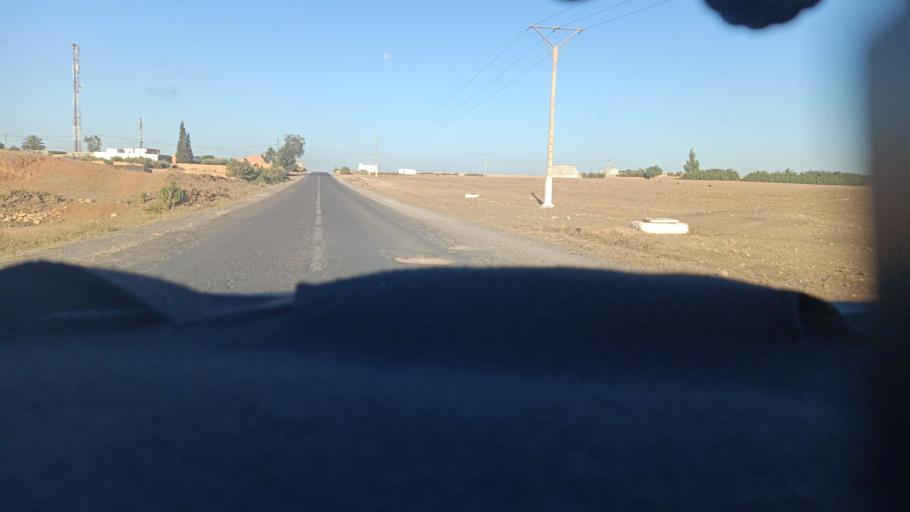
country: MA
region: Doukkala-Abda
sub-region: Safi
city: Youssoufia
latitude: 32.3705
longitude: -8.6741
